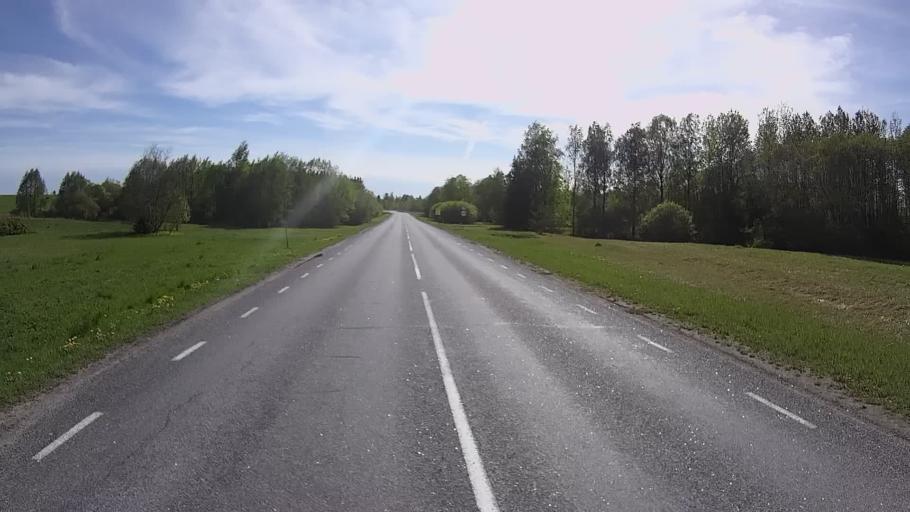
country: EE
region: Vorumaa
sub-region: Antsla vald
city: Vana-Antsla
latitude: 57.9276
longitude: 26.3406
